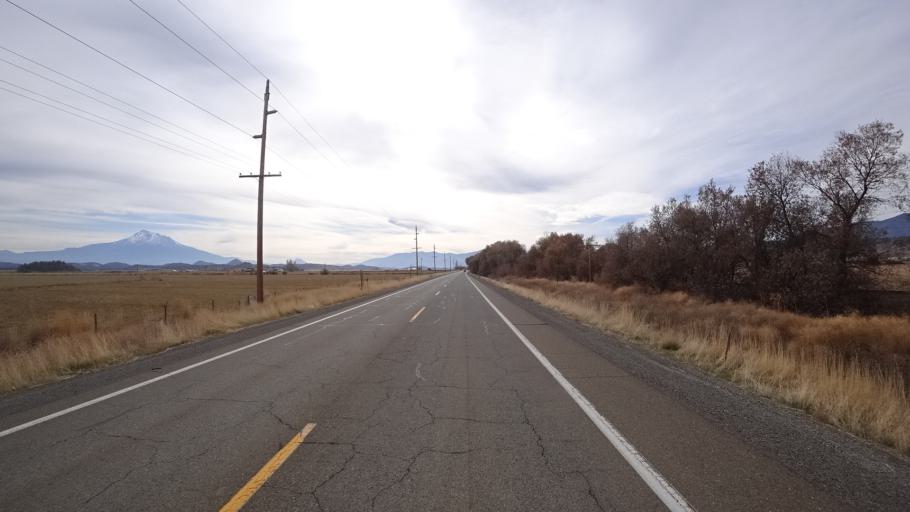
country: US
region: California
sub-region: Siskiyou County
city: Montague
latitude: 41.6534
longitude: -122.5203
